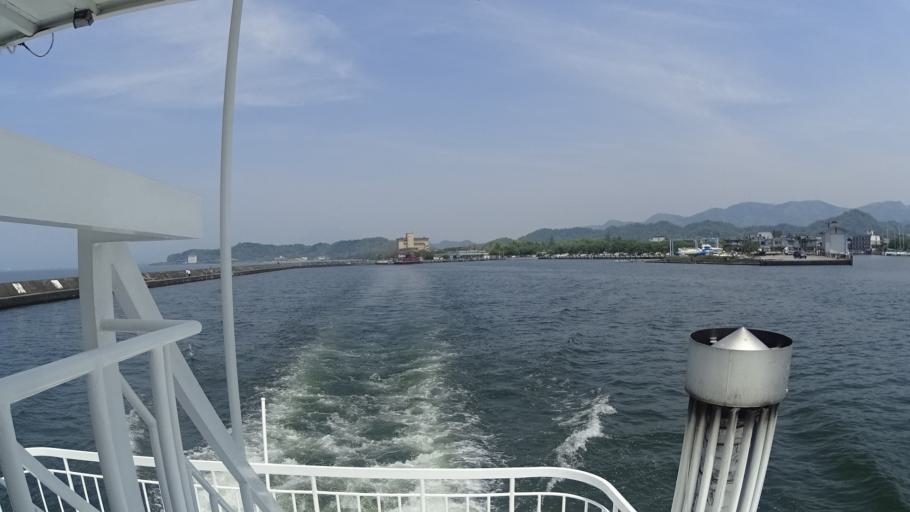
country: JP
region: Shiga Prefecture
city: Hikone
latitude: 35.2838
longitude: 136.2438
